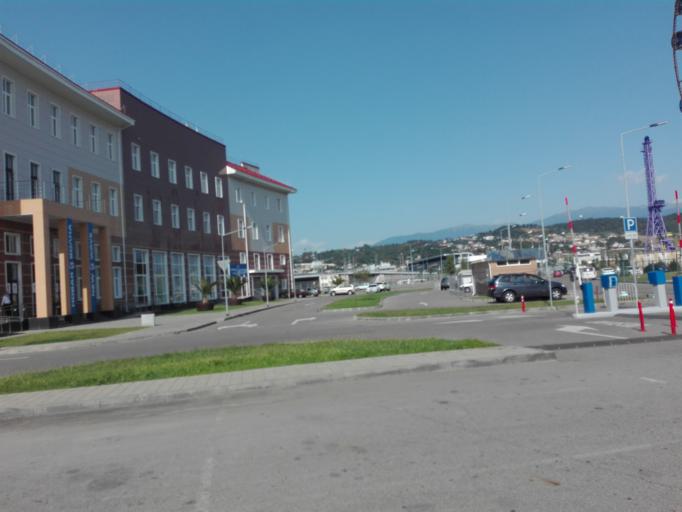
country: RU
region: Krasnodarskiy
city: Adler
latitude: 43.4044
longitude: 39.9614
